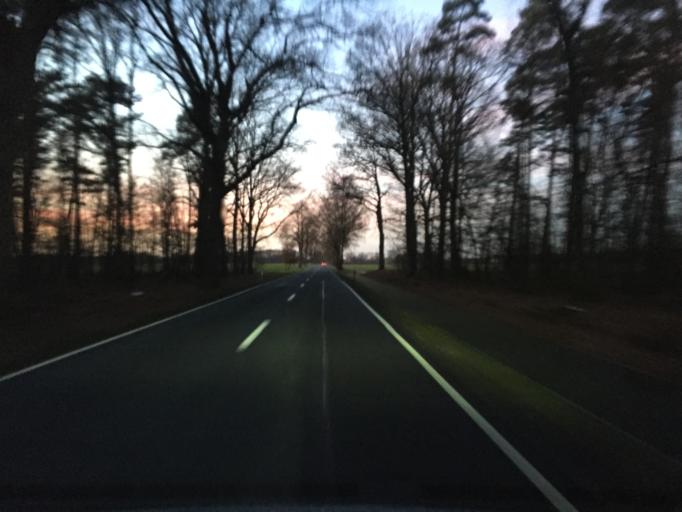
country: DE
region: Lower Saxony
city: Steyerberg
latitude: 52.5863
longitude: 8.9897
